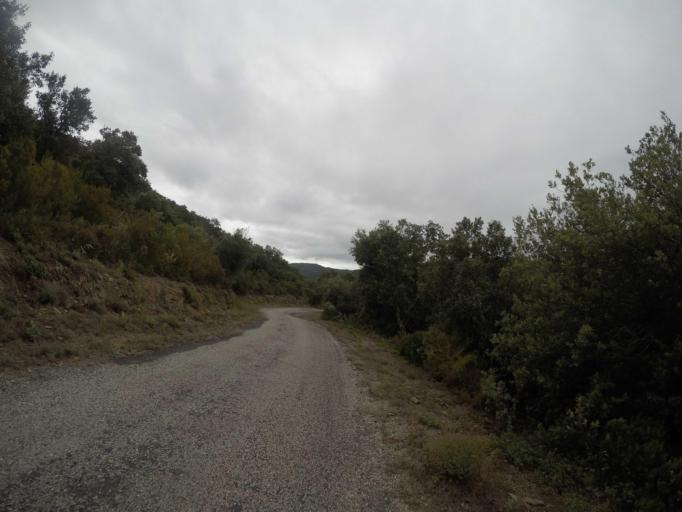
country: FR
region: Languedoc-Roussillon
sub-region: Departement des Pyrenees-Orientales
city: Ille-sur-Tet
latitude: 42.6149
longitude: 2.6046
